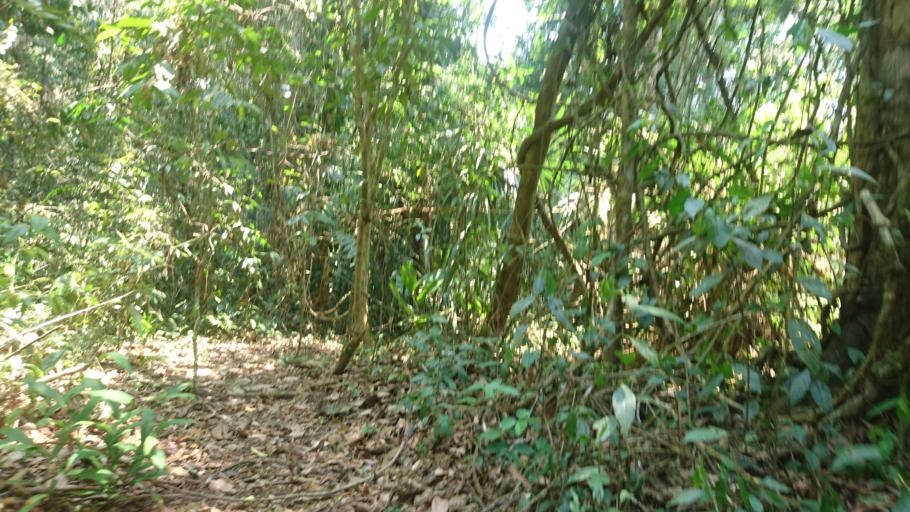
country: MX
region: Chiapas
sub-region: Marques de Comillas
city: Zamora Pico de Oro
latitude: 16.2474
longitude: -90.8308
